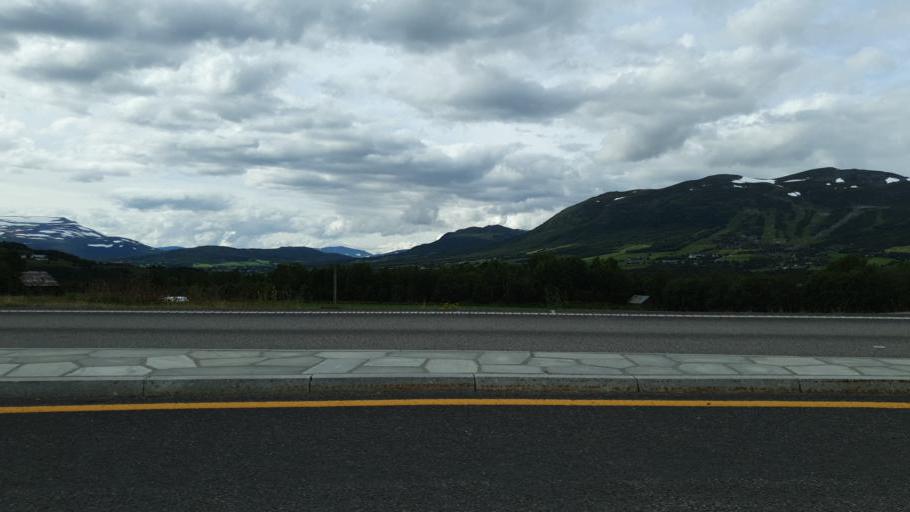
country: NO
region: Sor-Trondelag
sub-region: Oppdal
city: Oppdal
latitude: 62.5789
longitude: 9.6593
